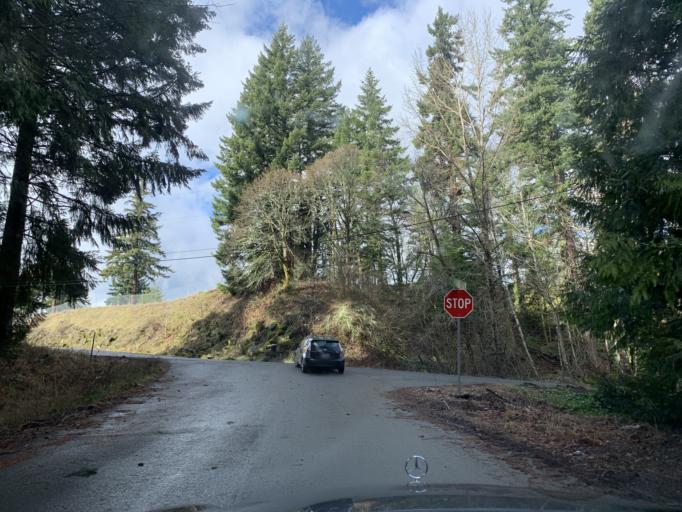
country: US
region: Washington
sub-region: Skamania County
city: Carson
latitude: 45.7263
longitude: -121.7992
